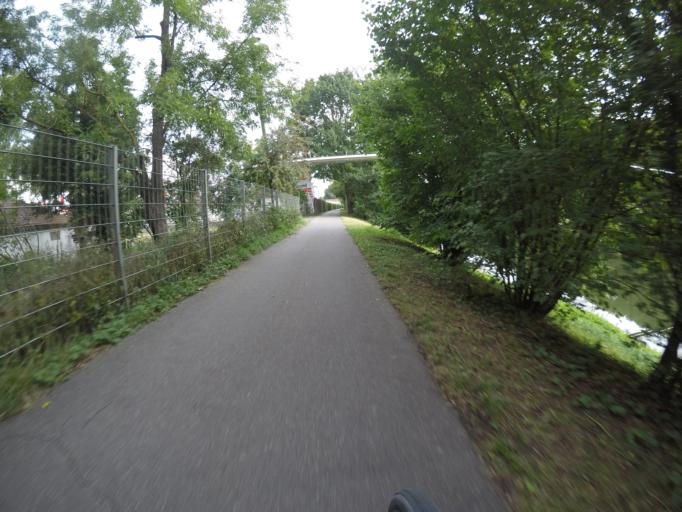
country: DE
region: Baden-Wuerttemberg
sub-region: Regierungsbezirk Stuttgart
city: Stuttgart Muehlhausen
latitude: 48.8531
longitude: 9.2487
